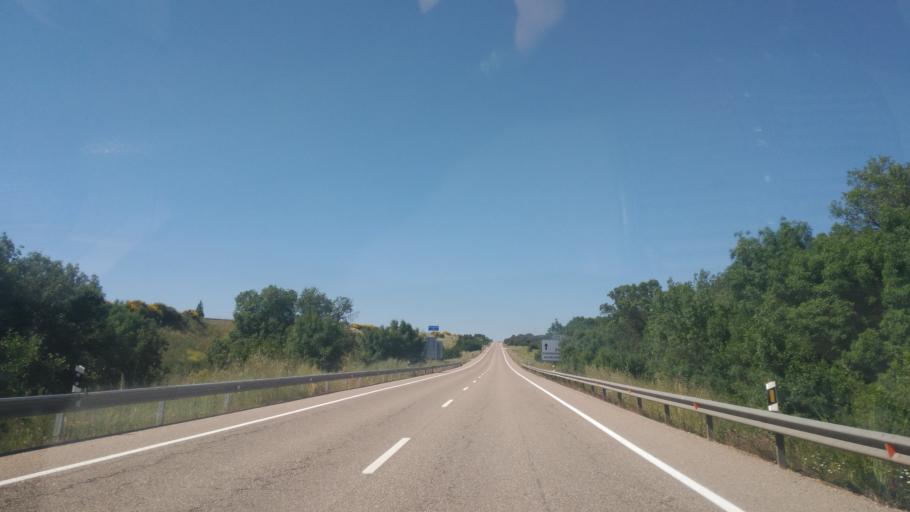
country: ES
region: Castille and Leon
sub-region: Provincia de Salamanca
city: Calzada de Valdunciel
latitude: 41.1325
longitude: -5.6967
